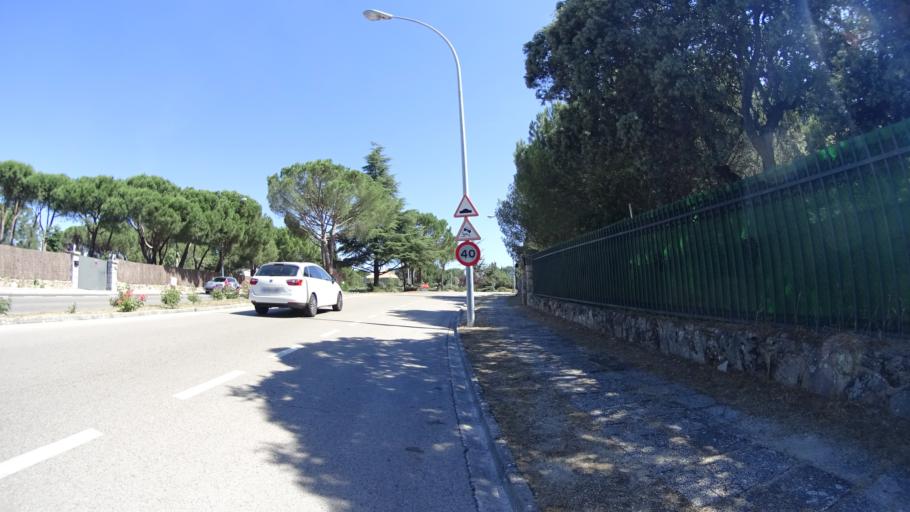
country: ES
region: Madrid
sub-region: Provincia de Madrid
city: Torrelodones
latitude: 40.5999
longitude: -3.9476
